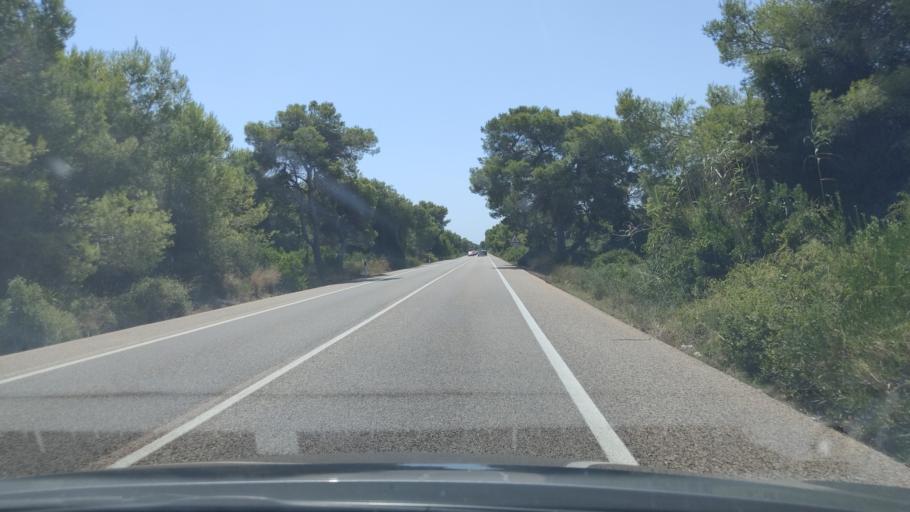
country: ES
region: Valencia
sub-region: Provincia de Valencia
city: Sollana
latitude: 39.3377
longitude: -0.3173
